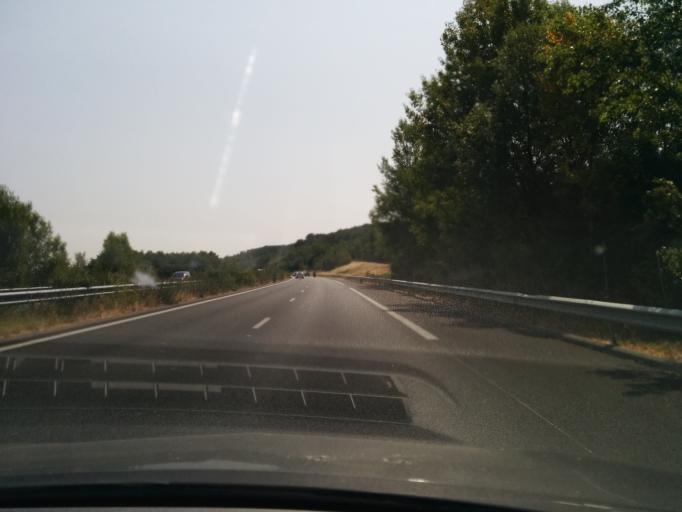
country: FR
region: Midi-Pyrenees
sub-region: Departement du Tarn
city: Lagrave
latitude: 43.8849
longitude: 1.9947
